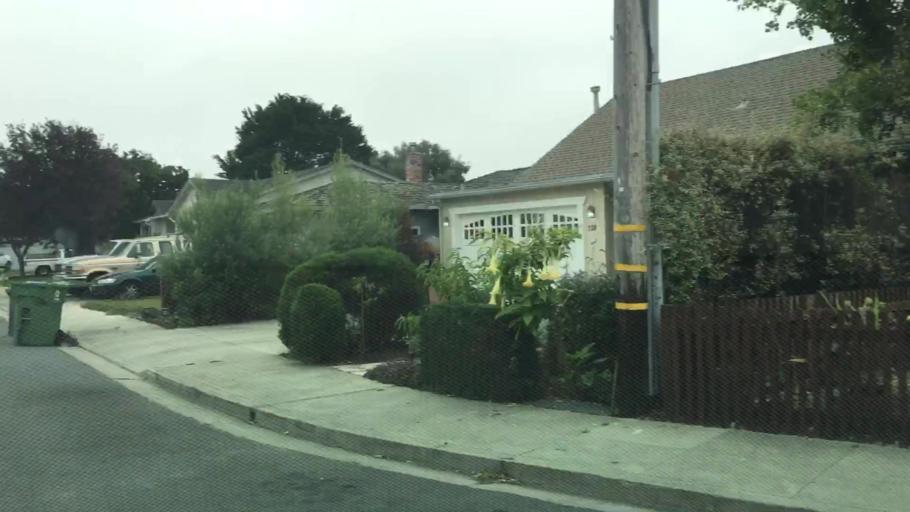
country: US
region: California
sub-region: San Mateo County
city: Half Moon Bay
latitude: 37.4597
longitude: -122.4280
